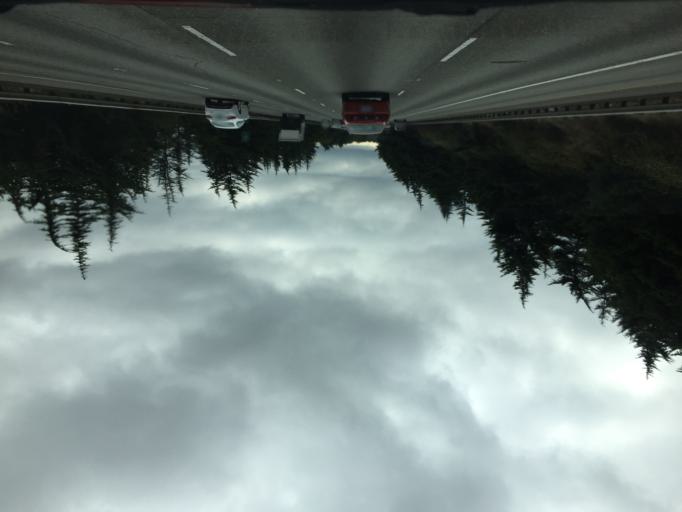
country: US
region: Washington
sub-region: King County
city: White Center
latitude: 47.5439
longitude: -122.3064
